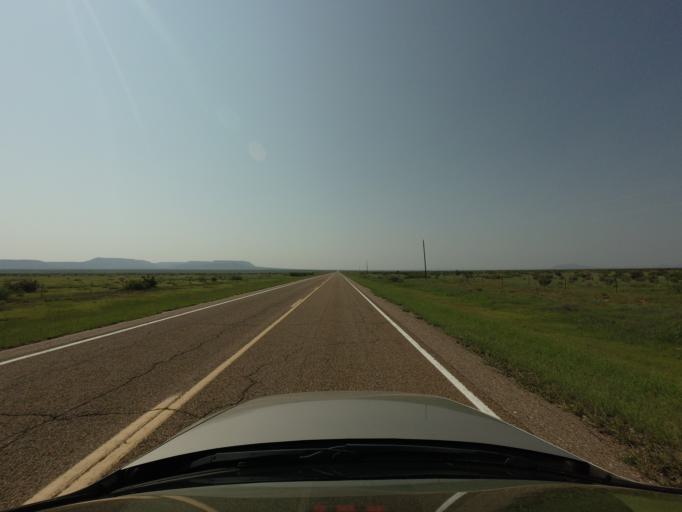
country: US
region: New Mexico
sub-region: Quay County
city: Tucumcari
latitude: 35.0500
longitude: -103.7376
